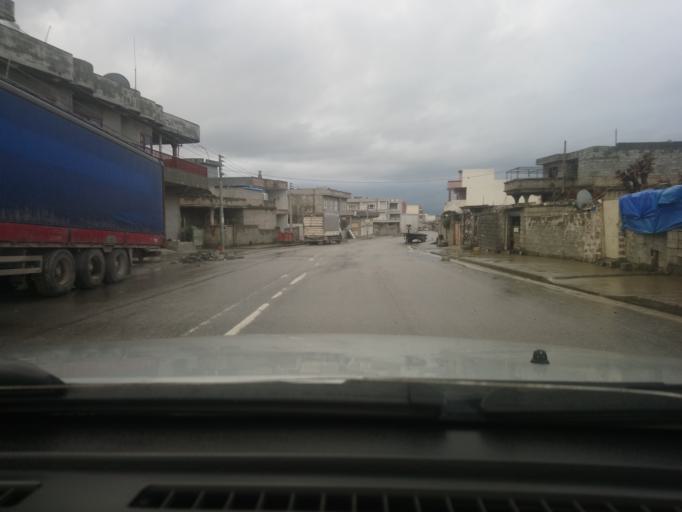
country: IQ
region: As Sulaymaniyah
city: Qeladize
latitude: 36.1783
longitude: 45.1425
